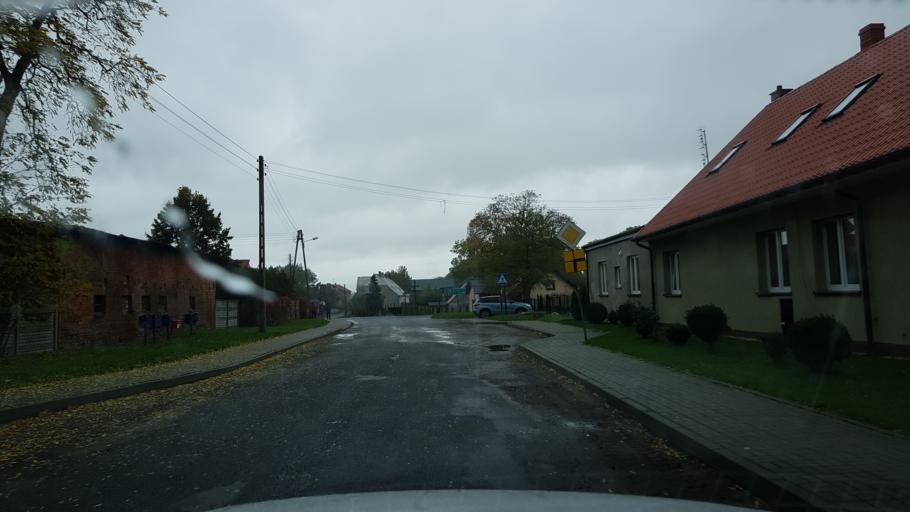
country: PL
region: West Pomeranian Voivodeship
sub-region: Powiat pyrzycki
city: Kozielice
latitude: 53.0317
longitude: 14.8518
